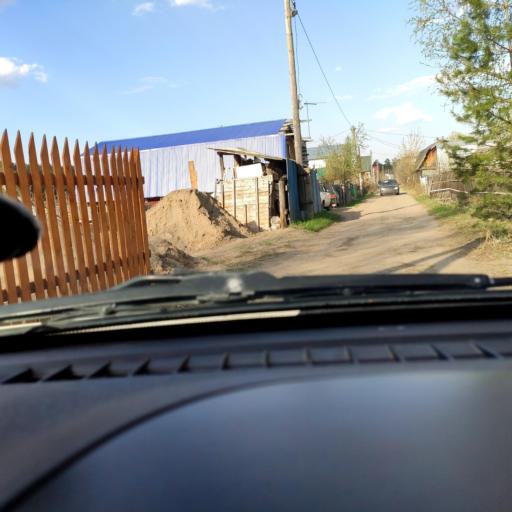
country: RU
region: Perm
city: Overyata
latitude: 58.0185
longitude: 55.9649
